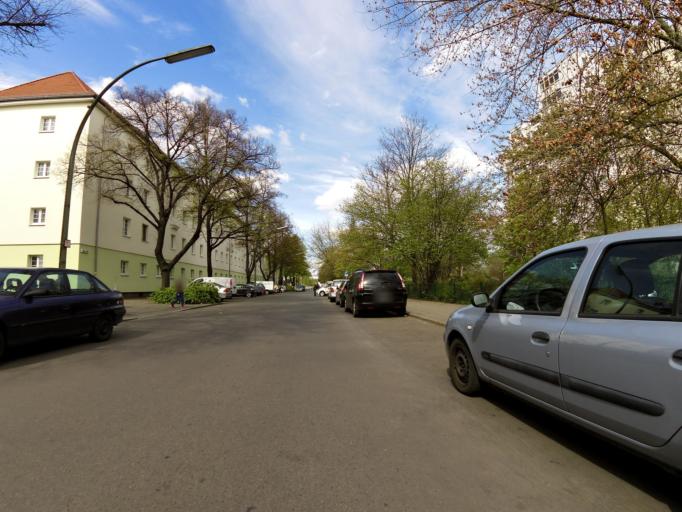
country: DE
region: Berlin
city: Plaenterwald
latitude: 52.4756
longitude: 13.4645
